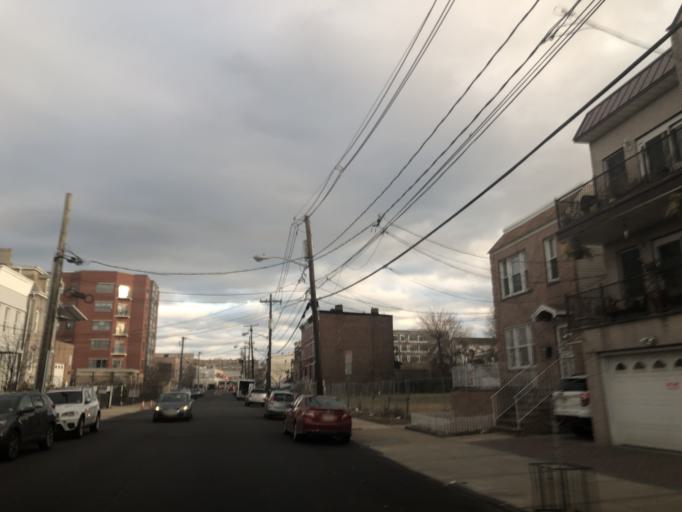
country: US
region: New Jersey
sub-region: Hudson County
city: Jersey City
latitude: 40.7145
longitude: -74.0924
